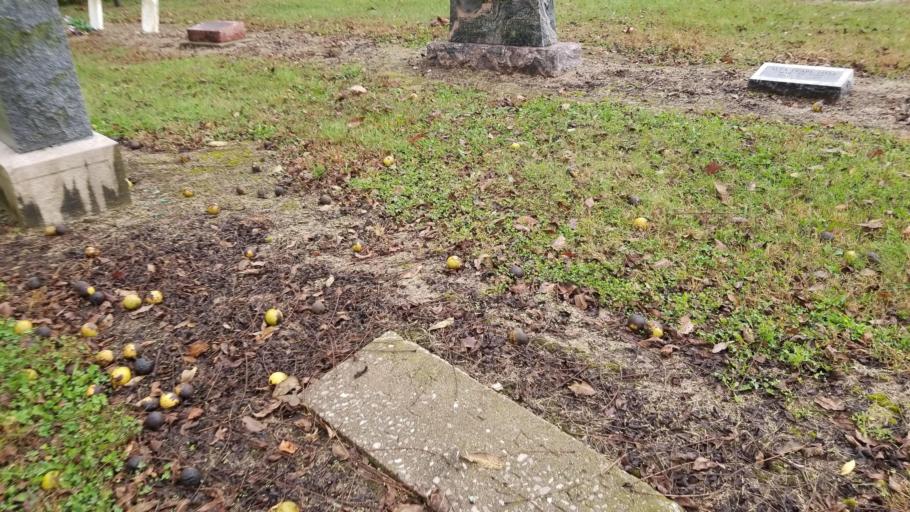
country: US
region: Illinois
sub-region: Saline County
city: Harrisburg
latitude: 37.8936
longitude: -88.6725
